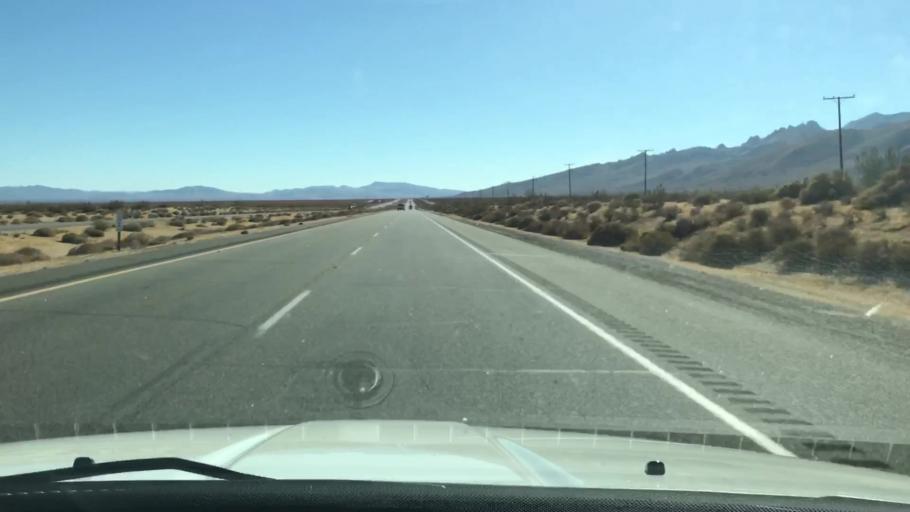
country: US
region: California
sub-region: Kern County
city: Inyokern
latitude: 35.7650
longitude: -117.8712
